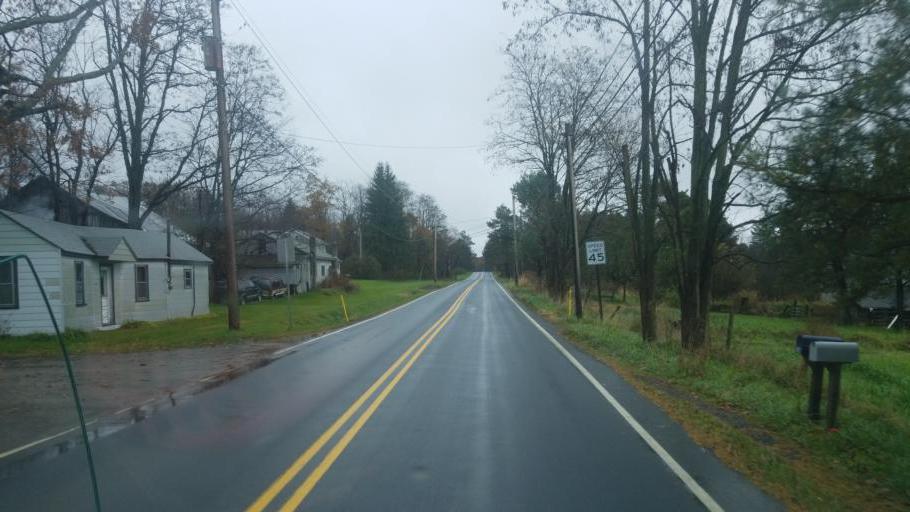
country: US
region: Pennsylvania
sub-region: Centre County
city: Milesburg
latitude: 41.0296
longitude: -77.9773
